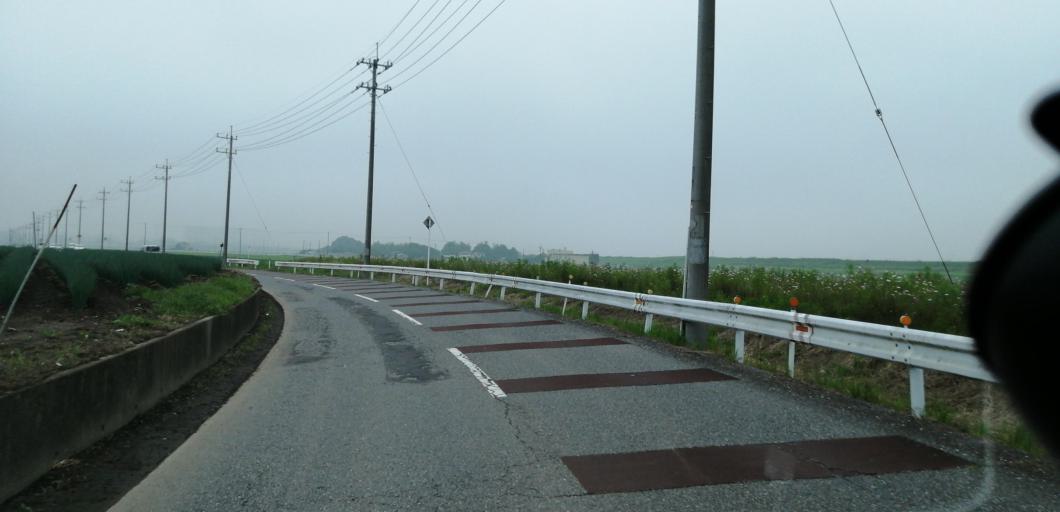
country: JP
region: Chiba
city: Noda
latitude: 35.9714
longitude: 139.9033
